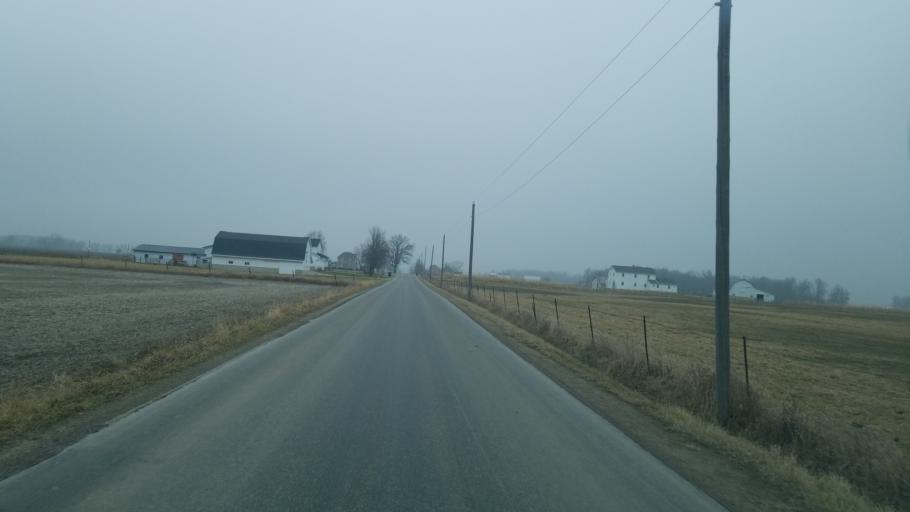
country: US
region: Indiana
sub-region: Adams County
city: Berne
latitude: 40.7204
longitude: -84.9751
